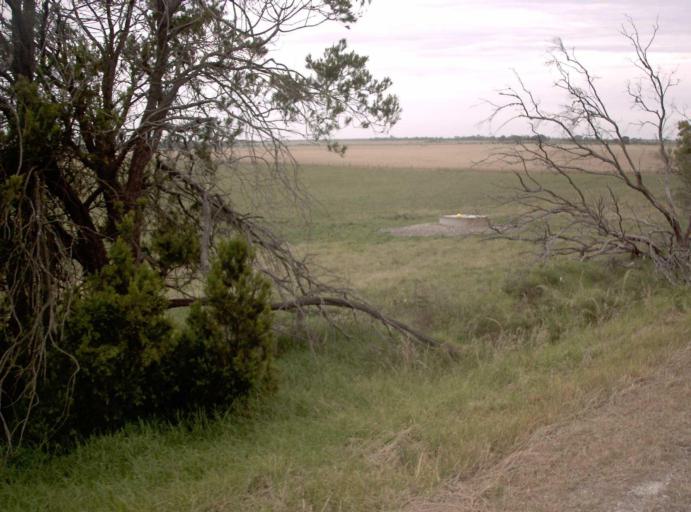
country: AU
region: Victoria
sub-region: Wellington
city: Sale
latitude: -38.1977
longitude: 147.3033
